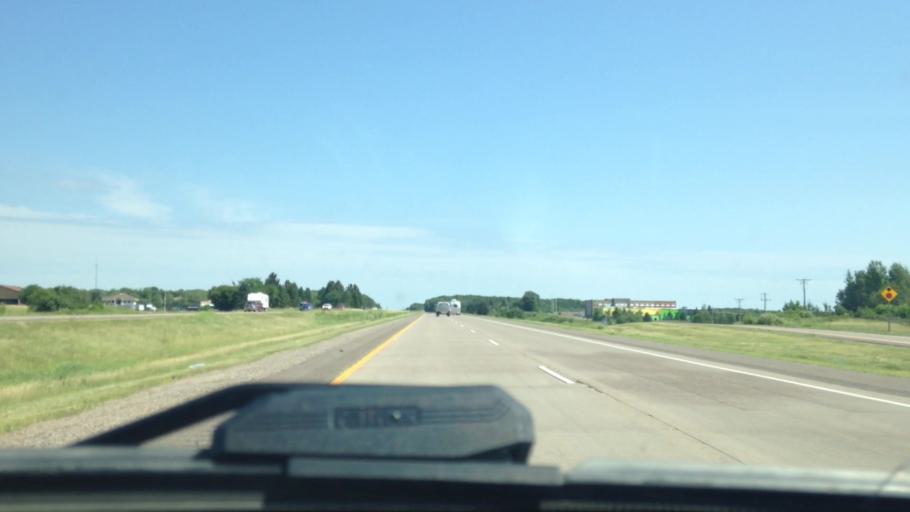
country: US
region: Wisconsin
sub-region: Barron County
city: Rice Lake
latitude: 45.5048
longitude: -91.7628
